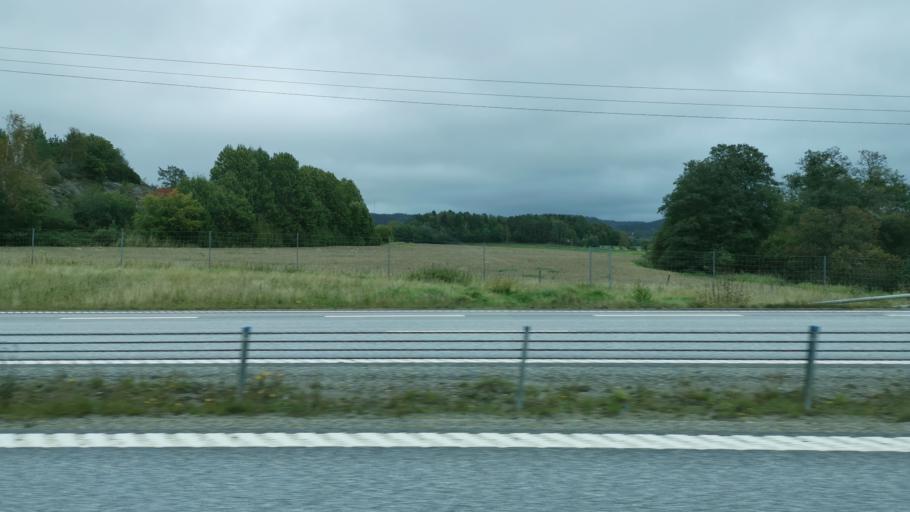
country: SE
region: Vaestra Goetaland
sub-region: Munkedals Kommun
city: Munkedal
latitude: 58.5189
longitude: 11.5497
